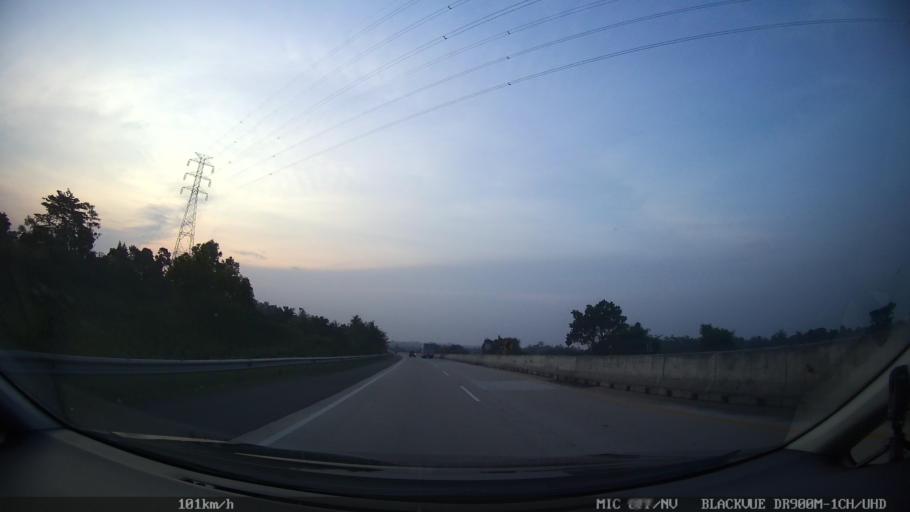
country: ID
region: Lampung
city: Pasuruan
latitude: -5.7194
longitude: 105.6619
